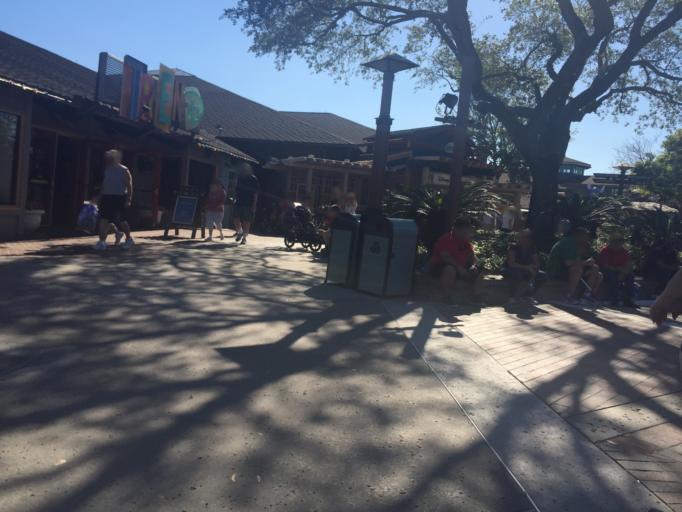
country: US
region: Florida
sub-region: Osceola County
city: Celebration
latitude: 28.3725
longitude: -81.5145
